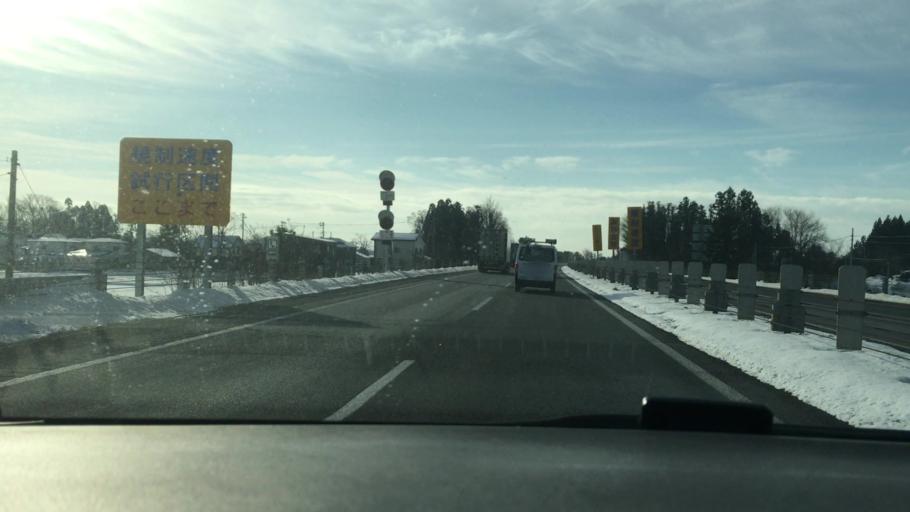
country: JP
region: Iwate
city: Hanamaki
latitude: 39.3996
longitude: 141.0926
